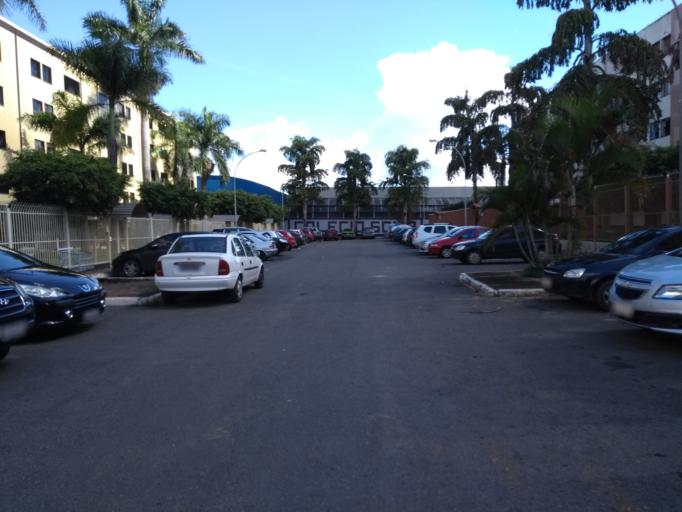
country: BR
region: Federal District
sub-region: Brasilia
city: Brasilia
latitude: -15.7942
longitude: -47.9395
